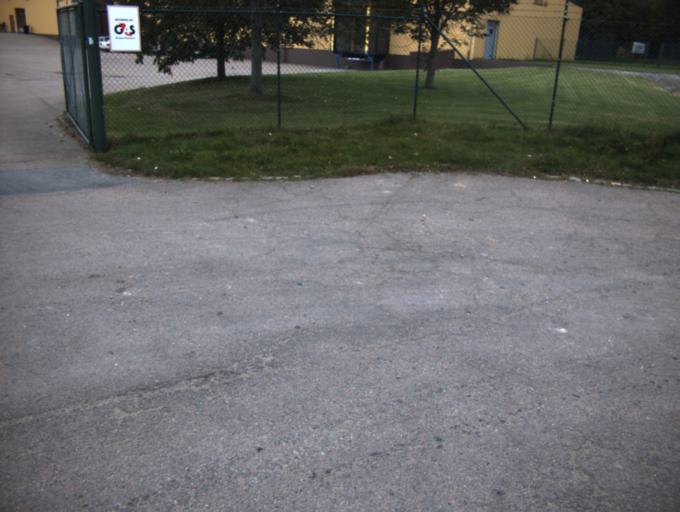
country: SE
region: Skane
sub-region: Helsingborg
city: Odakra
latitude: 56.0668
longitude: 12.7471
